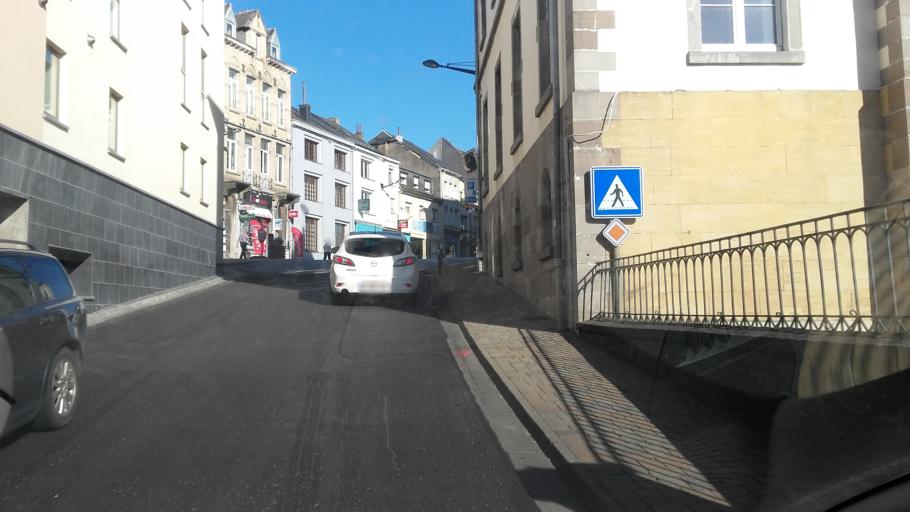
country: BE
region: Wallonia
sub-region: Province du Luxembourg
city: Neufchateau
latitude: 49.8400
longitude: 5.4356
